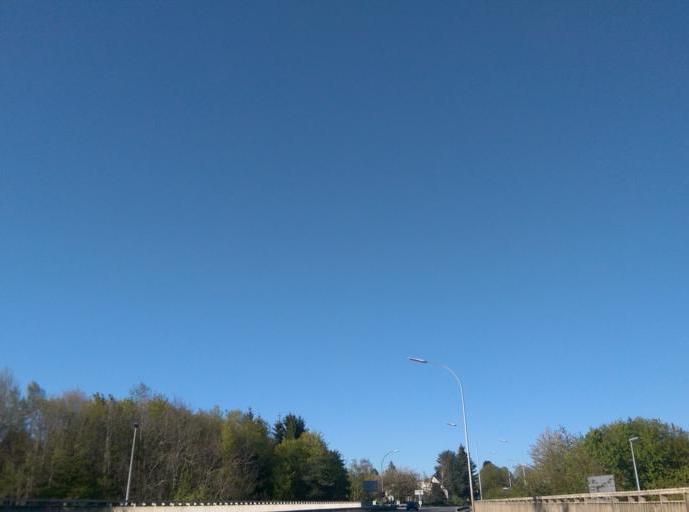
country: LU
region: Luxembourg
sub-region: Canton de Luxembourg
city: Sandweiler
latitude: 49.6421
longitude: 6.2176
